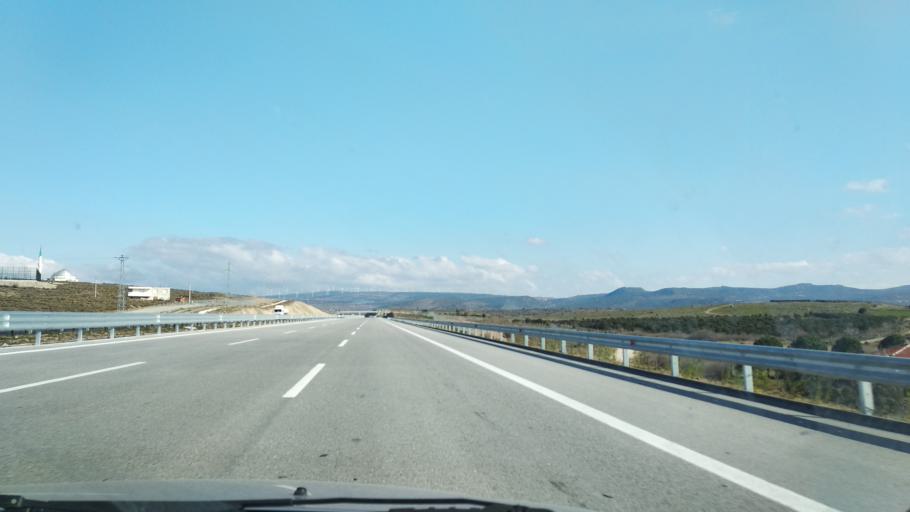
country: TR
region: Izmir
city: Yenisakran
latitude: 38.8549
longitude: 27.0606
